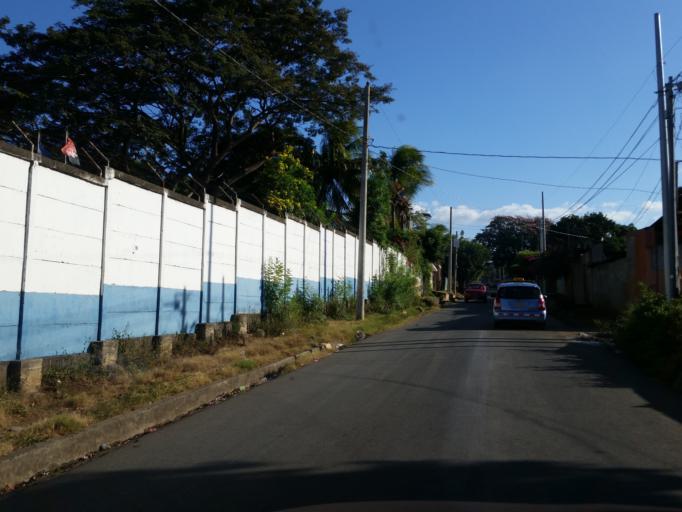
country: NI
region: Managua
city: Managua
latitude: 12.1137
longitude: -86.2935
